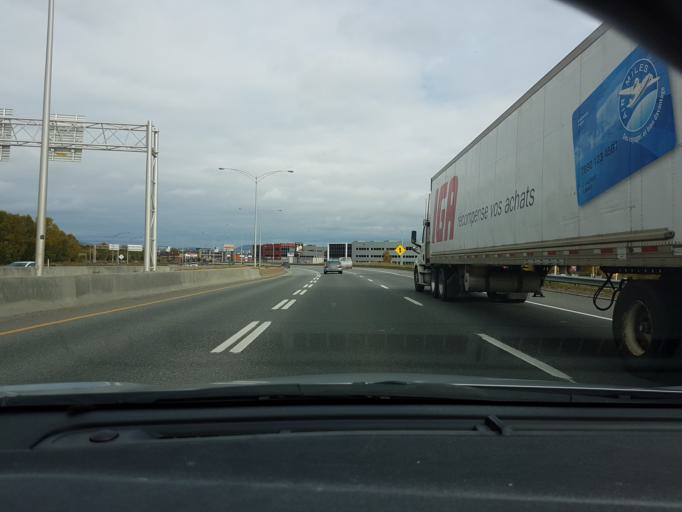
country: CA
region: Quebec
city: L'Ancienne-Lorette
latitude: 46.8123
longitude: -71.2889
